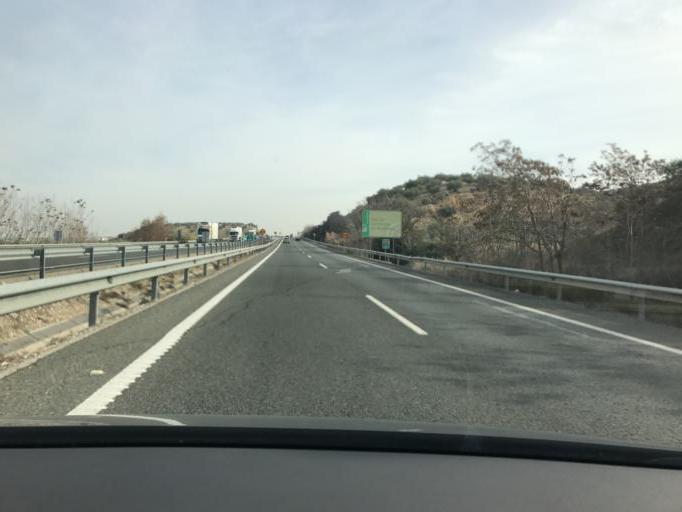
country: ES
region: Andalusia
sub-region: Provincia de Granada
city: Huetor-Tajar
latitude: 37.1811
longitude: -4.0512
